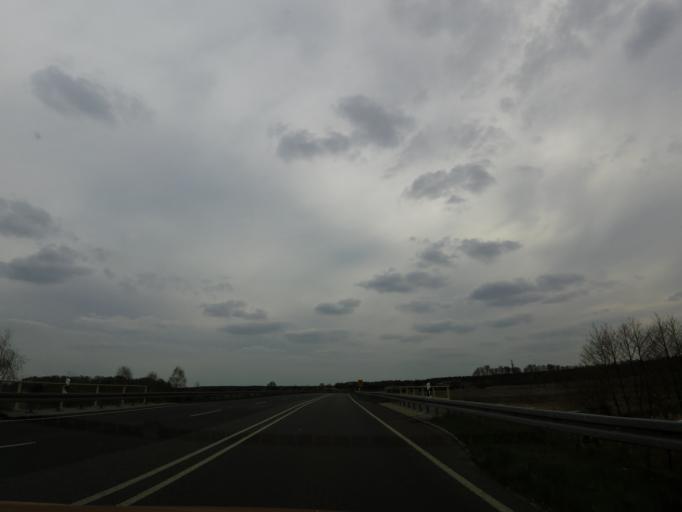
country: DE
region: Brandenburg
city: Mullrose
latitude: 52.2449
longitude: 14.3961
